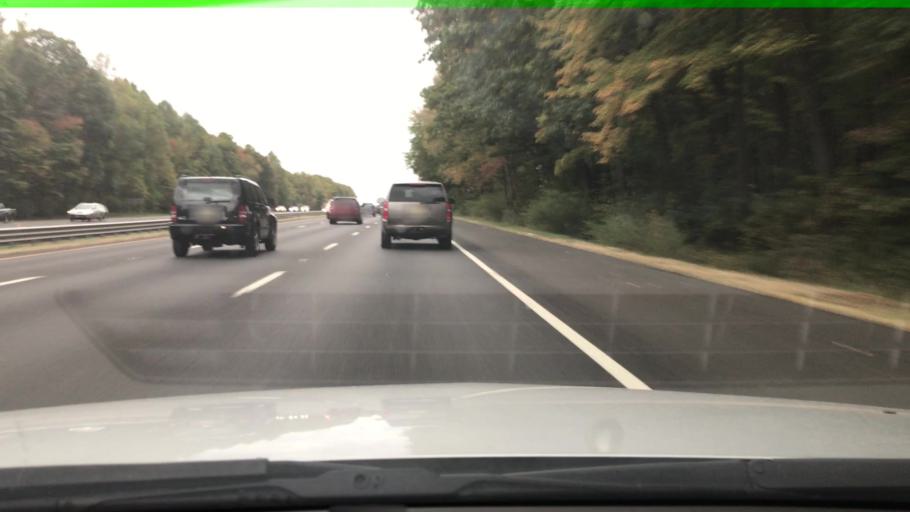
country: US
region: New Jersey
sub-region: Burlington County
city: Burlington
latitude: 40.0523
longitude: -74.8247
